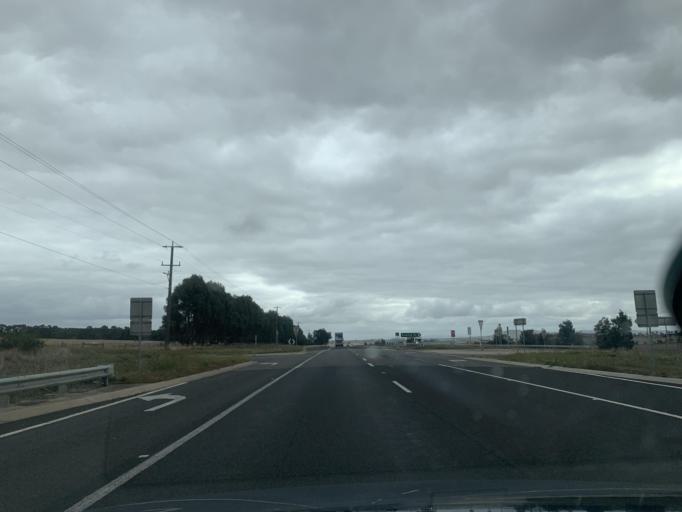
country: AU
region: Victoria
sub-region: Ballarat North
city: Newington
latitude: -37.4864
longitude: 143.7652
